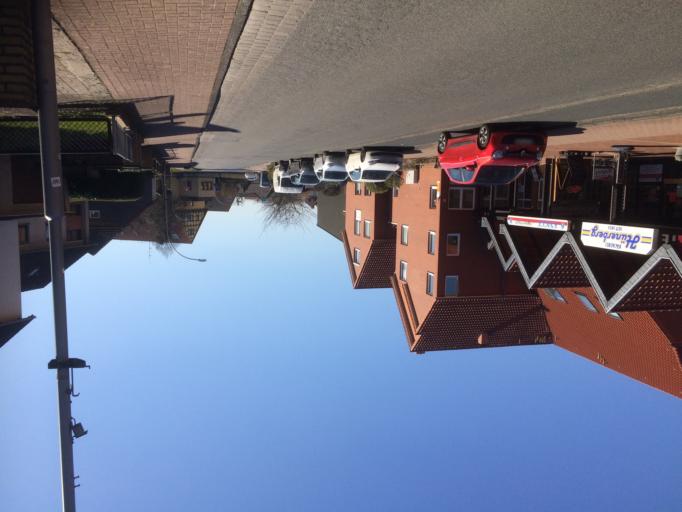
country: DE
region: Lower Saxony
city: Gehrden
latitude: 52.3112
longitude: 9.6027
